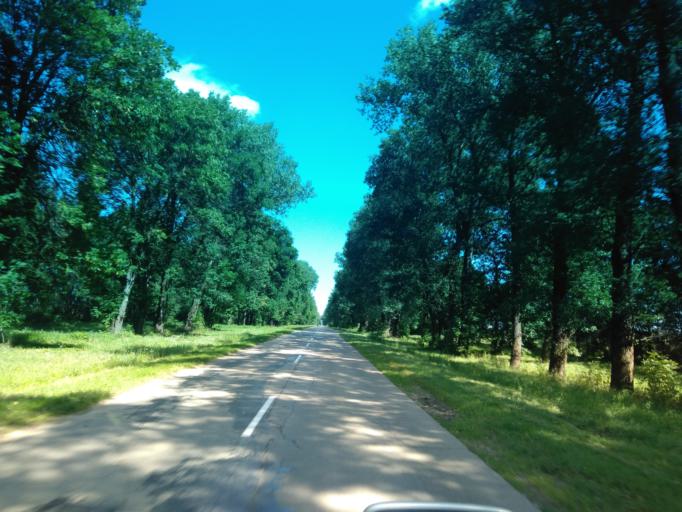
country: BY
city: Fanipol
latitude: 53.6600
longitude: 27.3244
